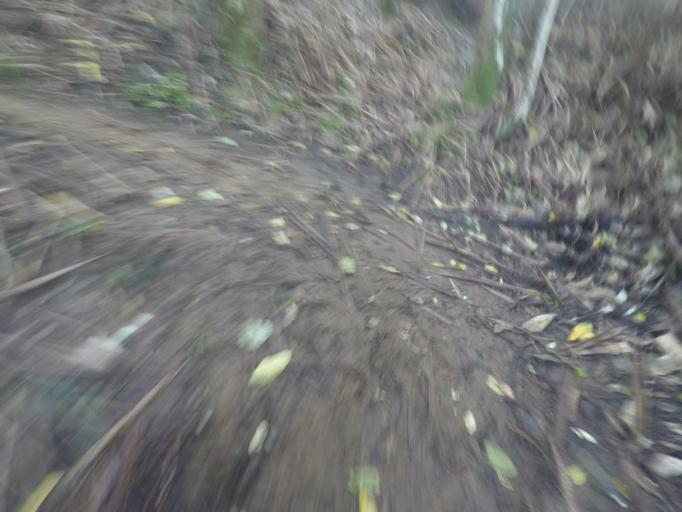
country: NZ
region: Auckland
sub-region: Auckland
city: Muriwai Beach
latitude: -36.8595
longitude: 174.4340
